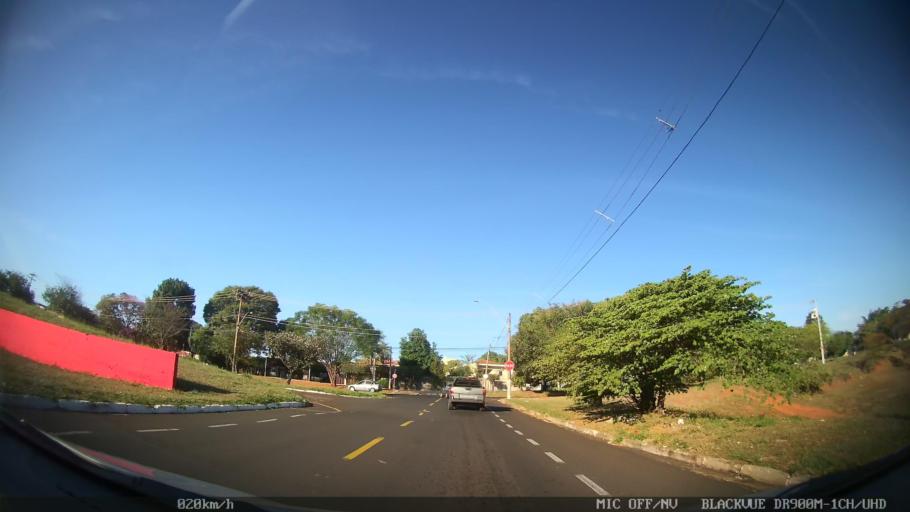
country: BR
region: Sao Paulo
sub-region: Sao Jose Do Rio Preto
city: Sao Jose do Rio Preto
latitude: -20.7988
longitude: -49.3581
